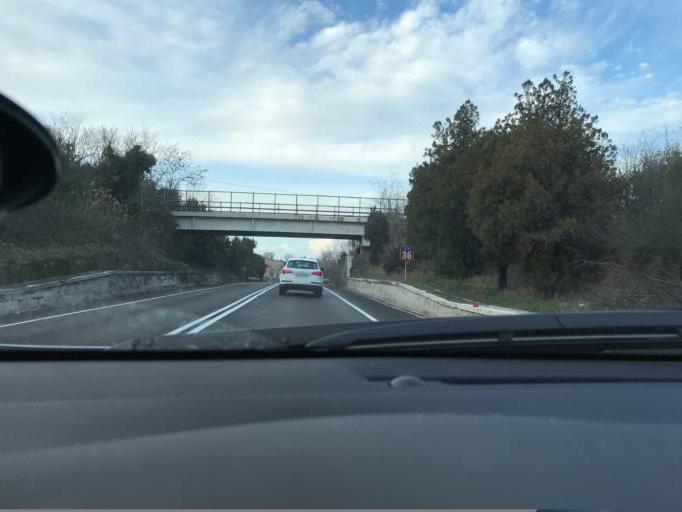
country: IT
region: The Marches
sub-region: Provincia di Ancona
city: Falconara Marittima
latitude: 43.6086
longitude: 13.4147
